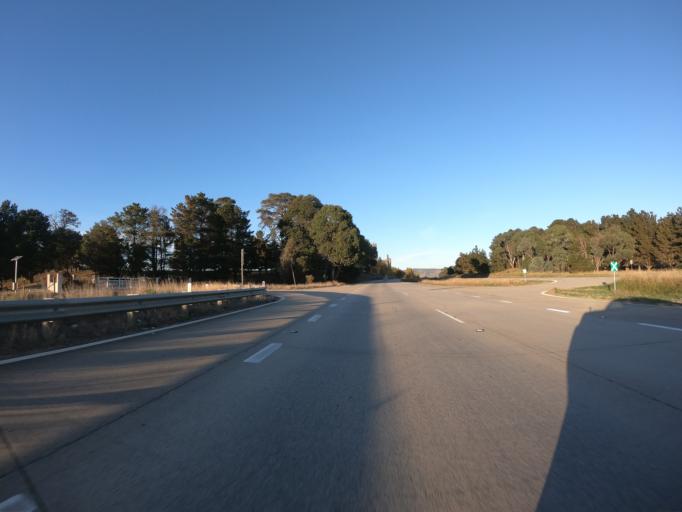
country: AU
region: New South Wales
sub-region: Yass Valley
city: Gundaroo
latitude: -34.9380
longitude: 149.4203
